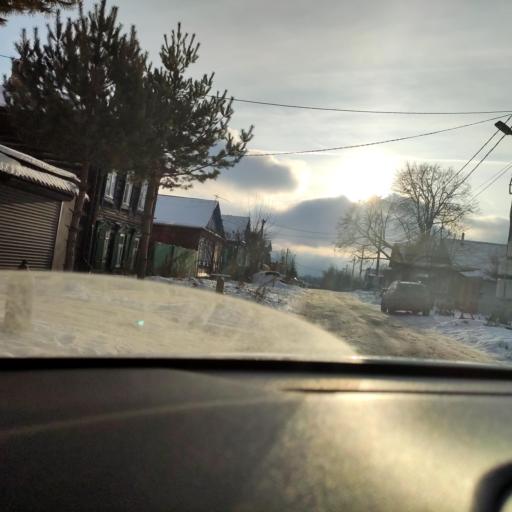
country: RU
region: Tatarstan
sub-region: Gorod Kazan'
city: Kazan
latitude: 55.7936
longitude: 49.0594
